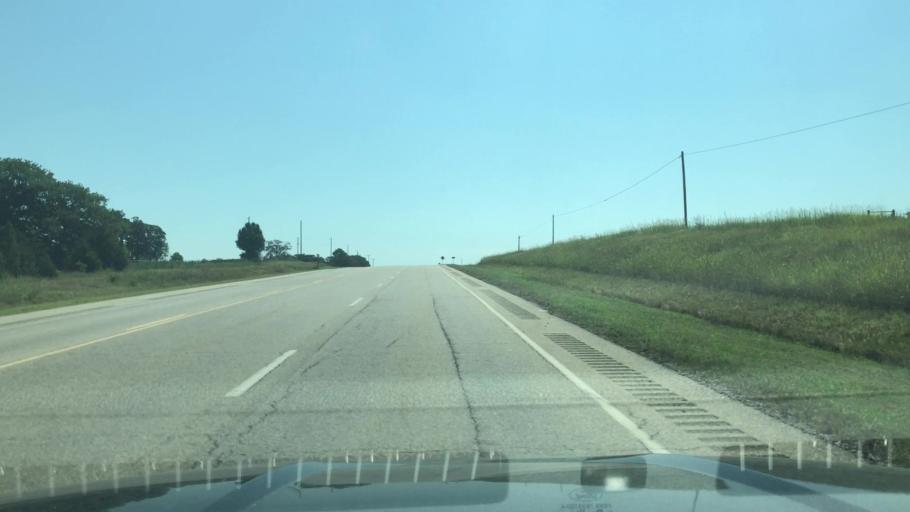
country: US
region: Oklahoma
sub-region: Creek County
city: Mannford
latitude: 36.0031
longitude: -96.4194
